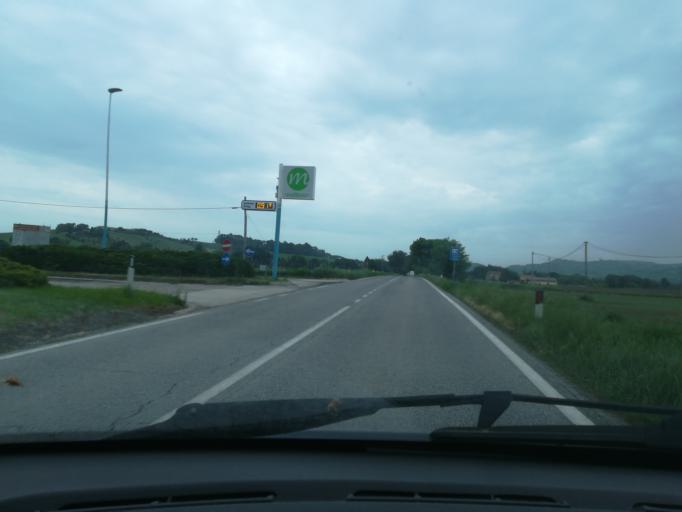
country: IT
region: The Marches
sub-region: Provincia di Macerata
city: Treia
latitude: 43.2706
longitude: 13.2750
